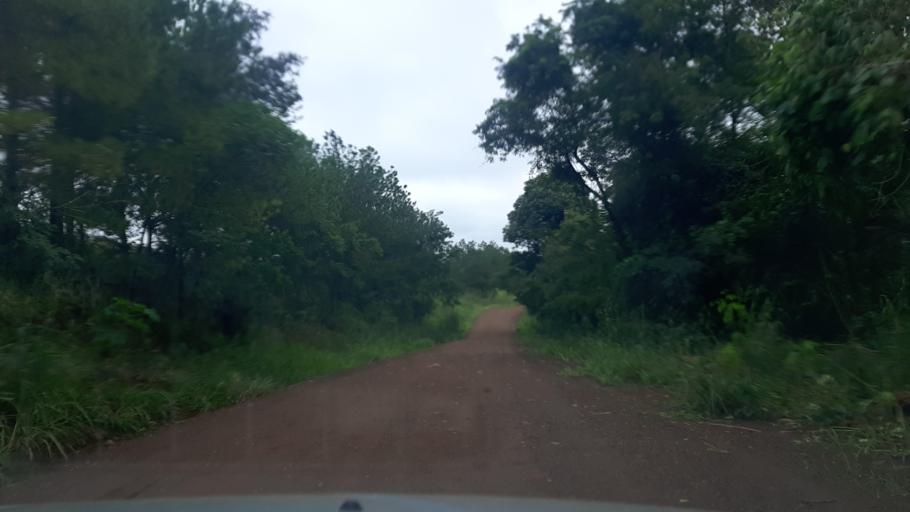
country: BR
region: Parana
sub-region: Ampere
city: Ampere
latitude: -26.0521
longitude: -53.5546
